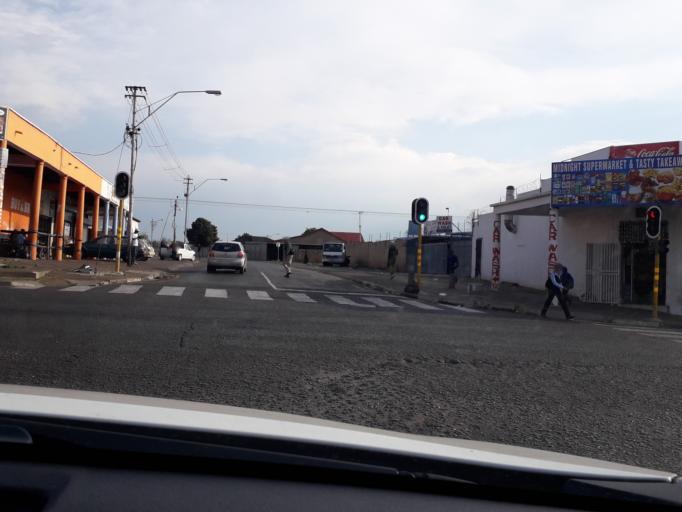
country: ZA
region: Gauteng
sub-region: City of Johannesburg Metropolitan Municipality
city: Johannesburg
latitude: -26.1757
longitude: 27.9673
